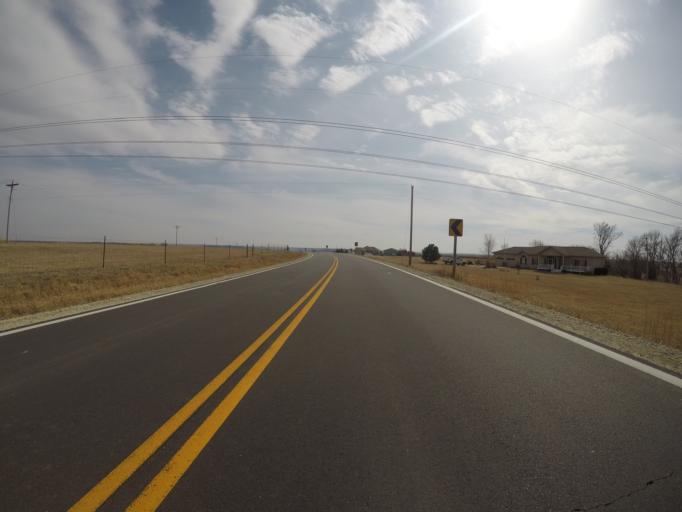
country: US
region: Kansas
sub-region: Geary County
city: Grandview Plaza
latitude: 39.0178
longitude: -96.7611
